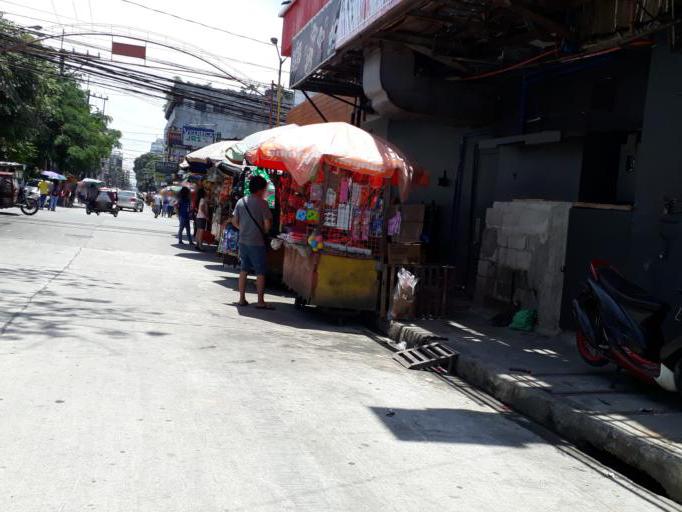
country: PH
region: Metro Manila
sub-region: Caloocan City
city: Niugan
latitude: 14.6533
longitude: 120.9847
